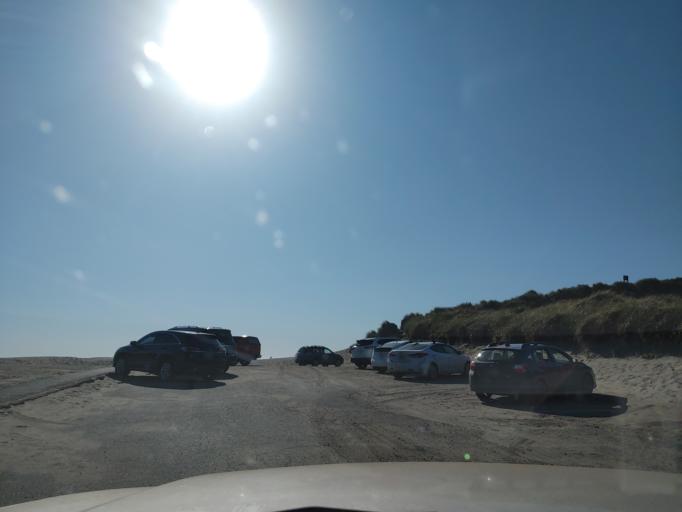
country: US
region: Oregon
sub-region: Clatsop County
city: Warrenton
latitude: 46.1783
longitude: -123.9786
